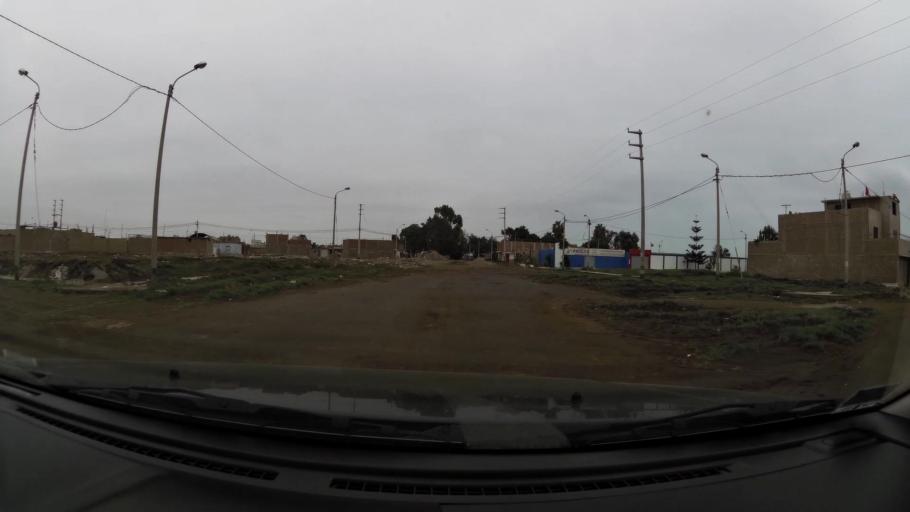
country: PE
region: Ica
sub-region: Provincia de Pisco
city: Pisco
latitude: -13.7123
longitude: -76.2124
